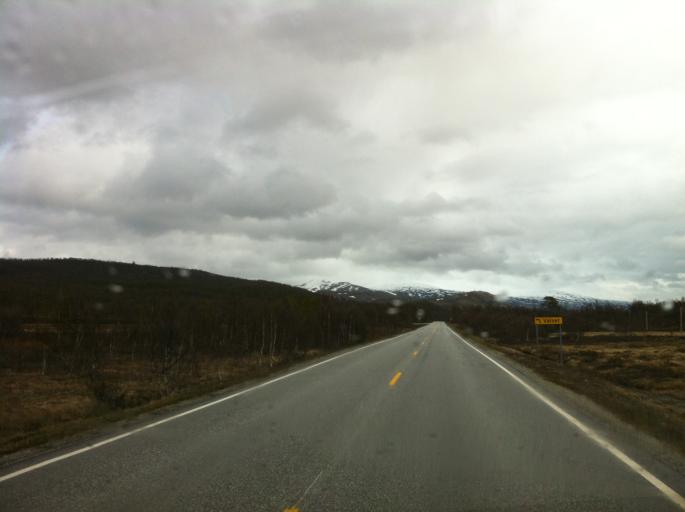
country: NO
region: Sor-Trondelag
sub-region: Roros
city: Roros
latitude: 62.6006
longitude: 11.6740
